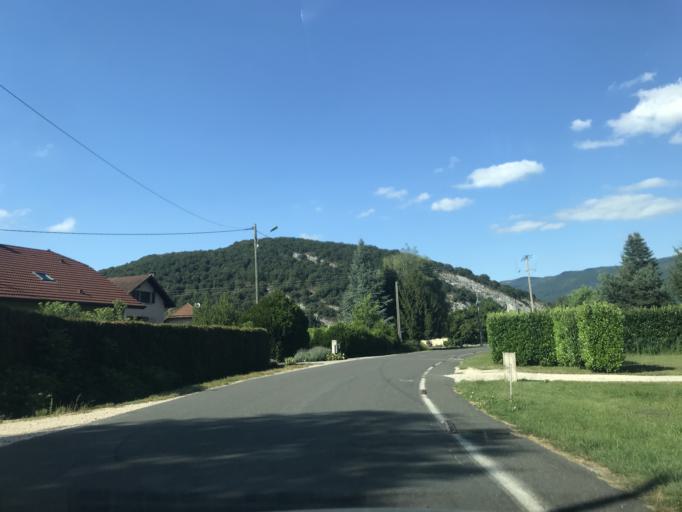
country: FR
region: Rhone-Alpes
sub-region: Departement de l'Ain
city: Culoz
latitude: 45.8211
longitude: 5.8022
